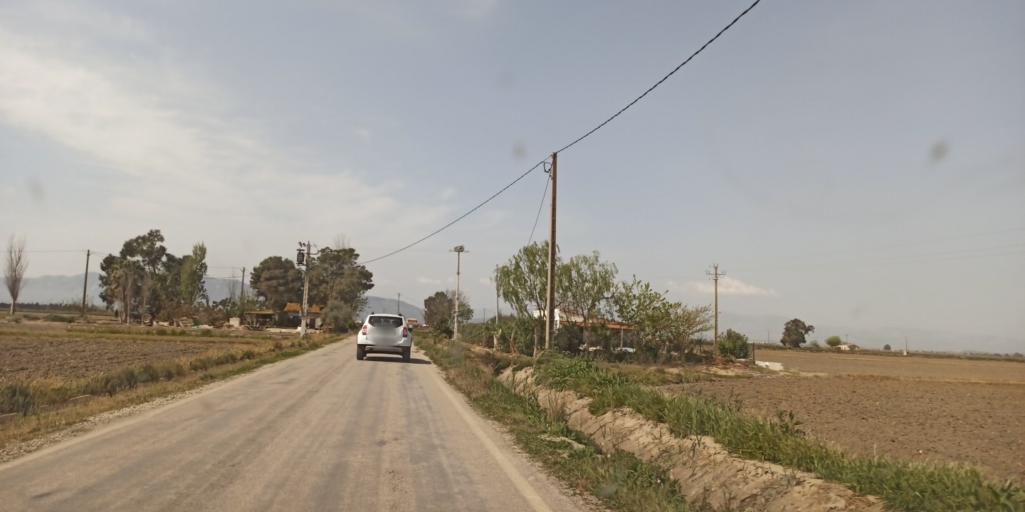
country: ES
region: Catalonia
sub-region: Provincia de Tarragona
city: Deltebre
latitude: 40.6465
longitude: 0.7116
